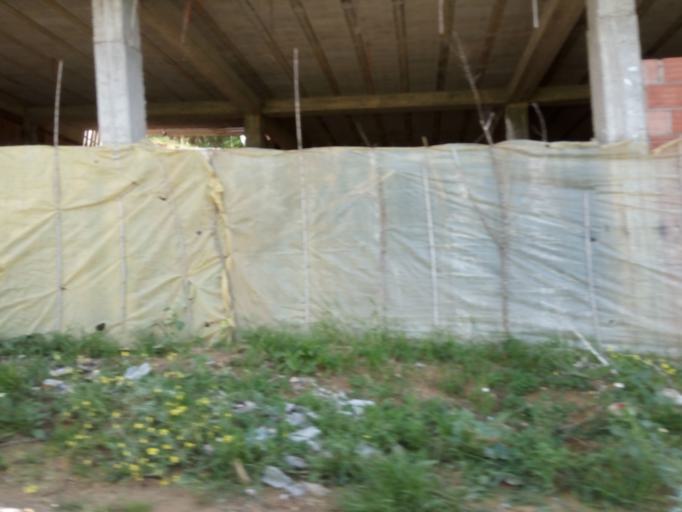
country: DZ
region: Tipaza
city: Hadjout
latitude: 36.3739
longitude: 2.4952
